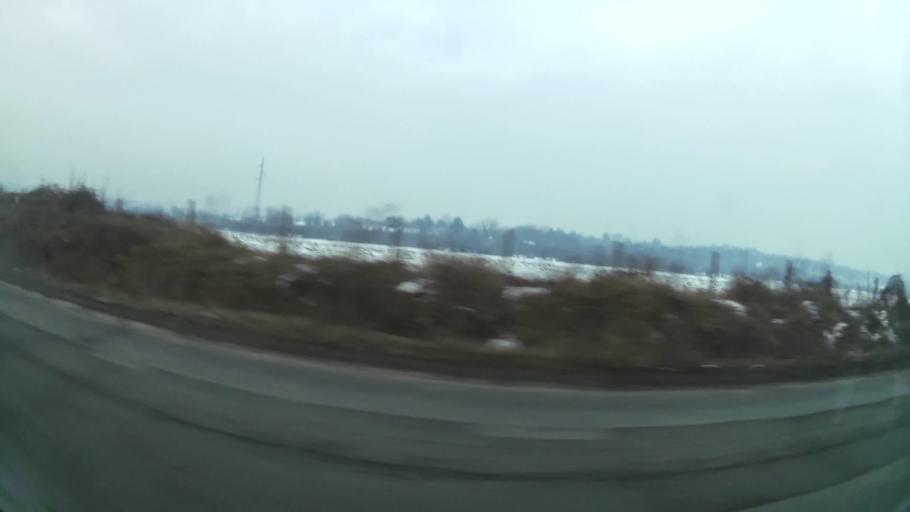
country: MK
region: Suto Orizari
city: Suto Orizare
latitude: 42.0227
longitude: 21.4095
